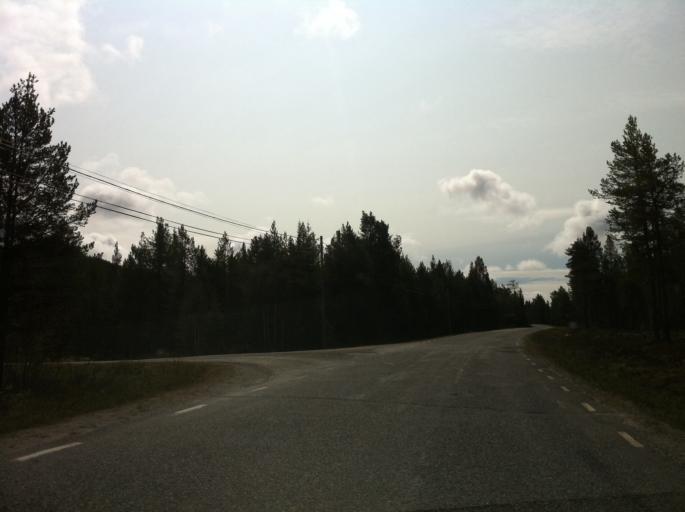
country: NO
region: Hedmark
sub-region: Engerdal
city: Engerdal
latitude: 62.4375
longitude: 12.6786
